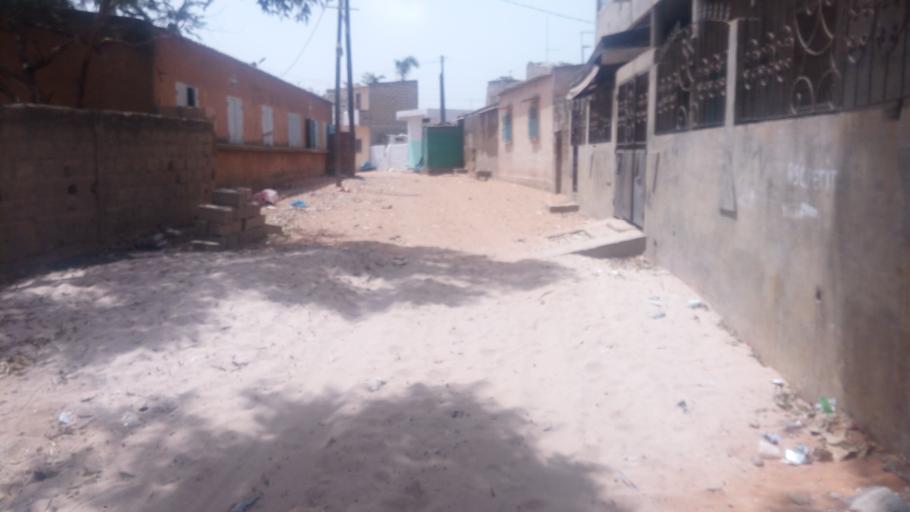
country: SN
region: Dakar
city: Pikine
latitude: 14.7952
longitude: -17.3382
